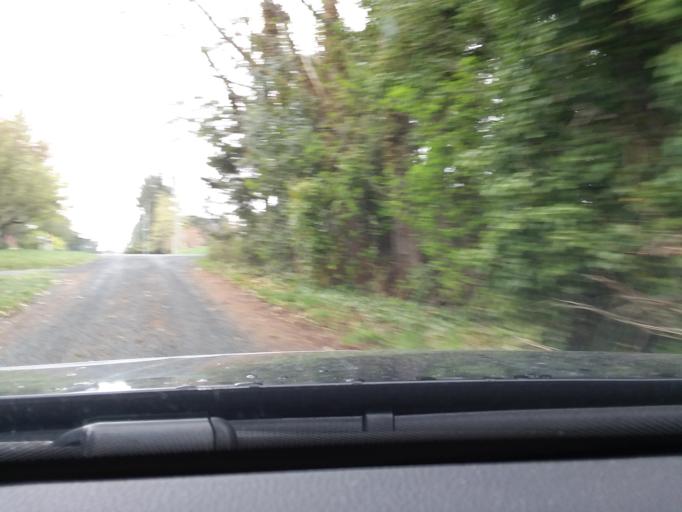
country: CA
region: British Columbia
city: North Saanich
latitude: 48.5508
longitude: -123.4008
